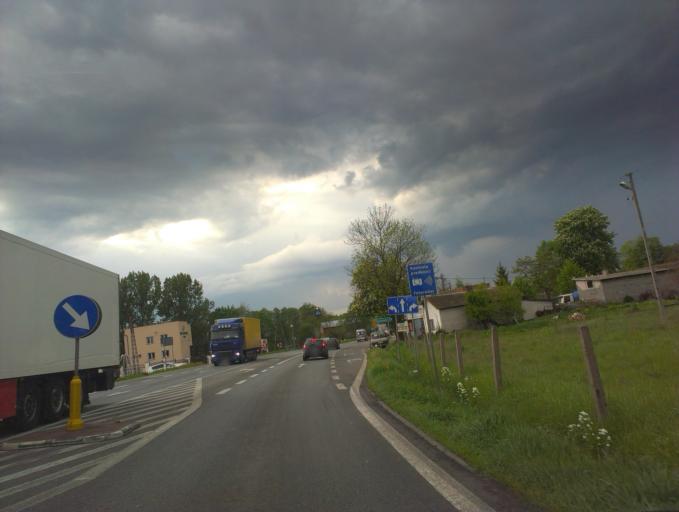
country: PL
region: Masovian Voivodeship
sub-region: Powiat grojecki
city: Pniewy
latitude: 51.8950
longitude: 20.7835
